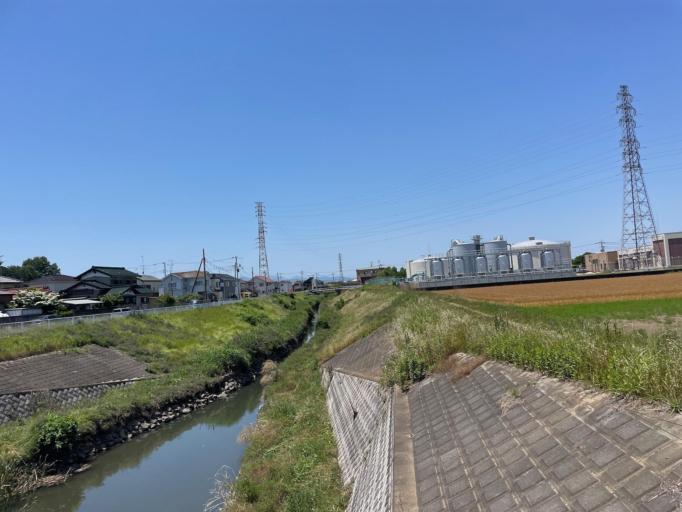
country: JP
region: Saitama
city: Fukayacho
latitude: 36.2055
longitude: 139.2929
